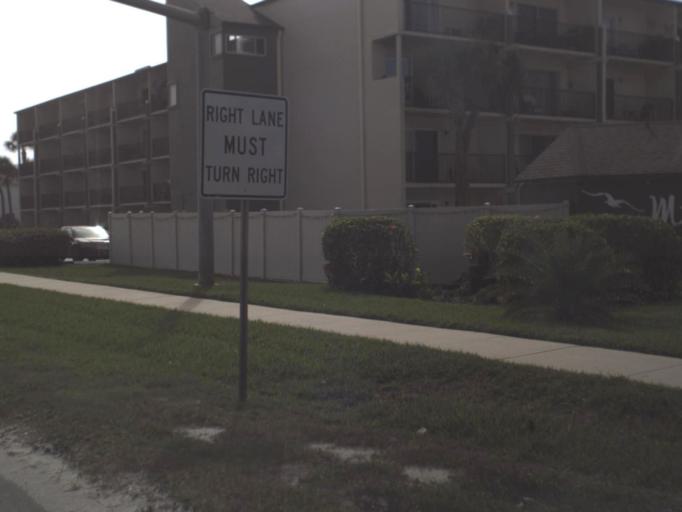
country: US
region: Florida
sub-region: Volusia County
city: Edgewater
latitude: 29.0089
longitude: -80.8793
